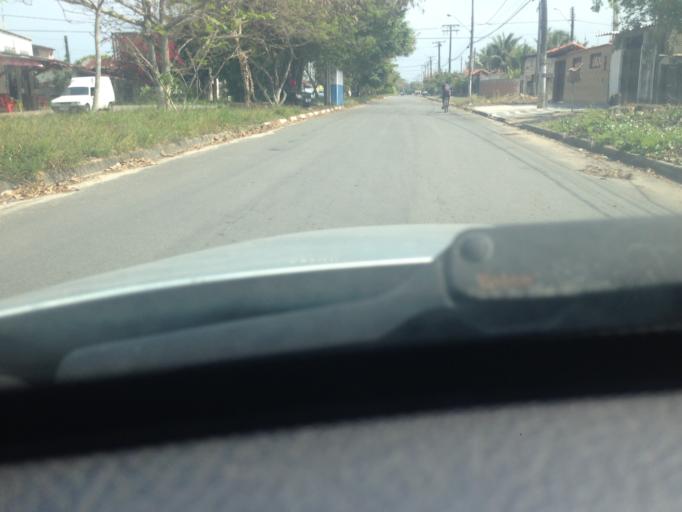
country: BR
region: Sao Paulo
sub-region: Itanhaem
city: Itanhaem
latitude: -24.2257
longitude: -46.8669
